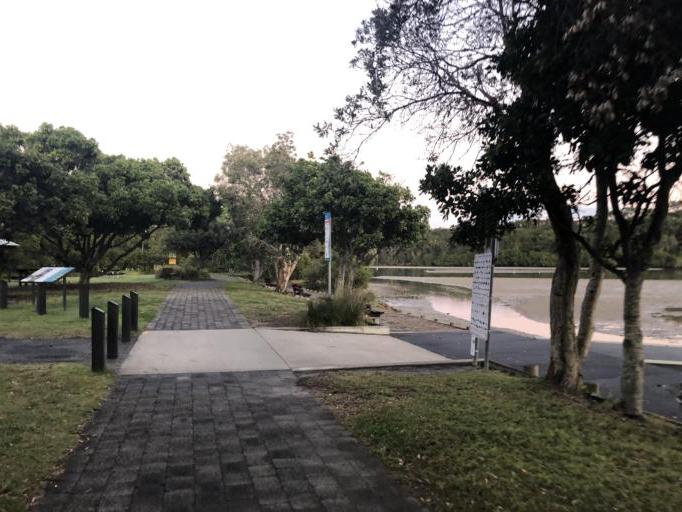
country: AU
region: New South Wales
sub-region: Coffs Harbour
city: Coffs Harbour
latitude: -30.2985
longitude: 153.1357
